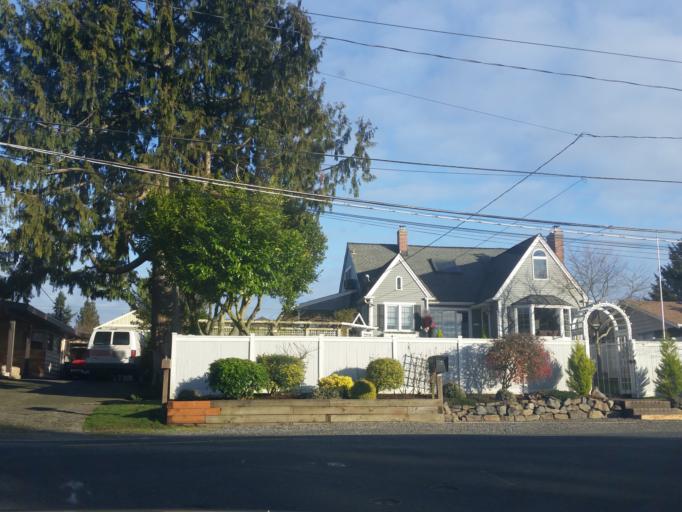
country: US
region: Washington
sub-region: King County
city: Shoreline
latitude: 47.6990
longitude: -122.3769
